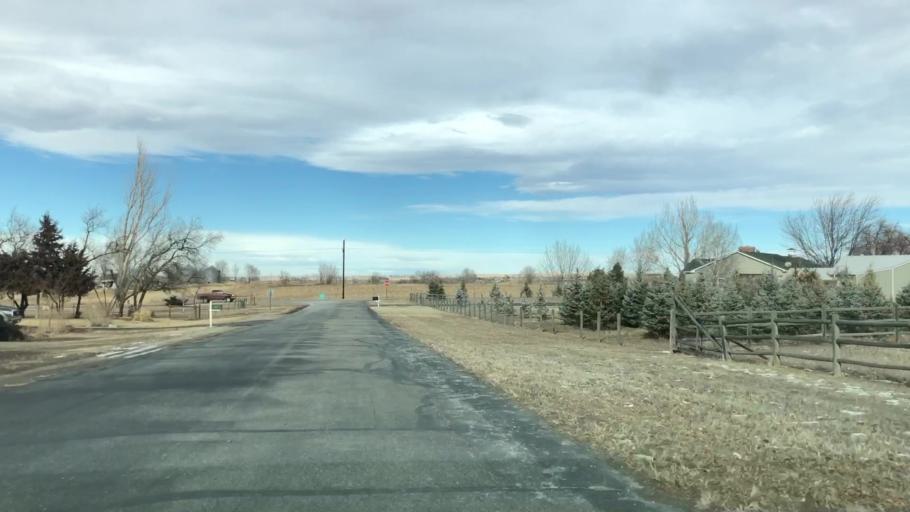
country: US
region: Colorado
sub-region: Weld County
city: Windsor
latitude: 40.5366
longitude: -104.9346
